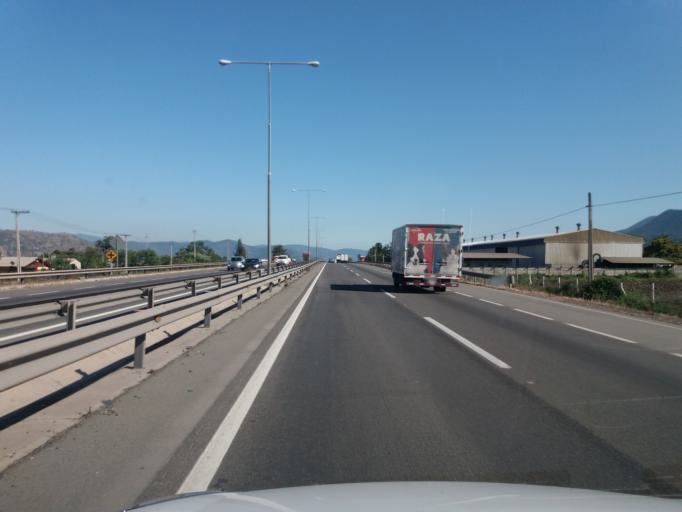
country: CL
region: Valparaiso
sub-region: Provincia de Quillota
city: Hacienda La Calera
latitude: -32.8164
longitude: -71.1426
